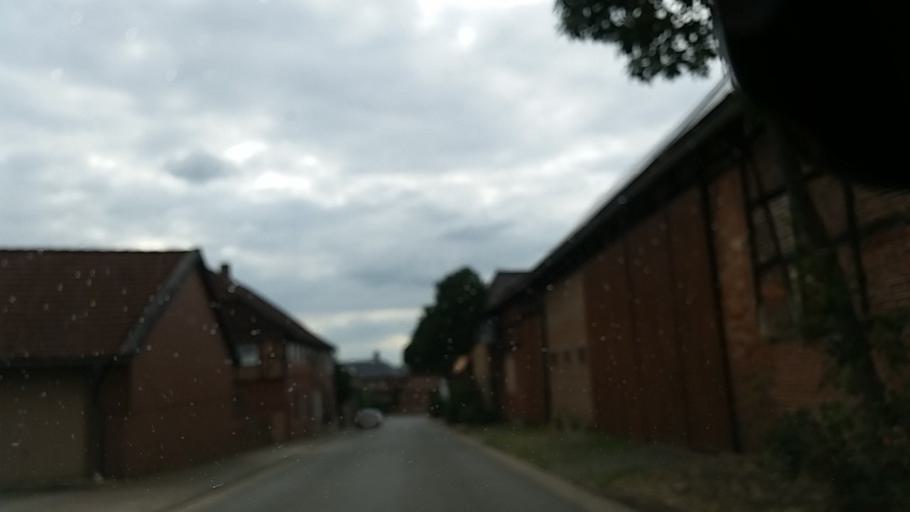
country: DE
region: Lower Saxony
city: Lehre
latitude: 52.3525
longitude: 10.7385
